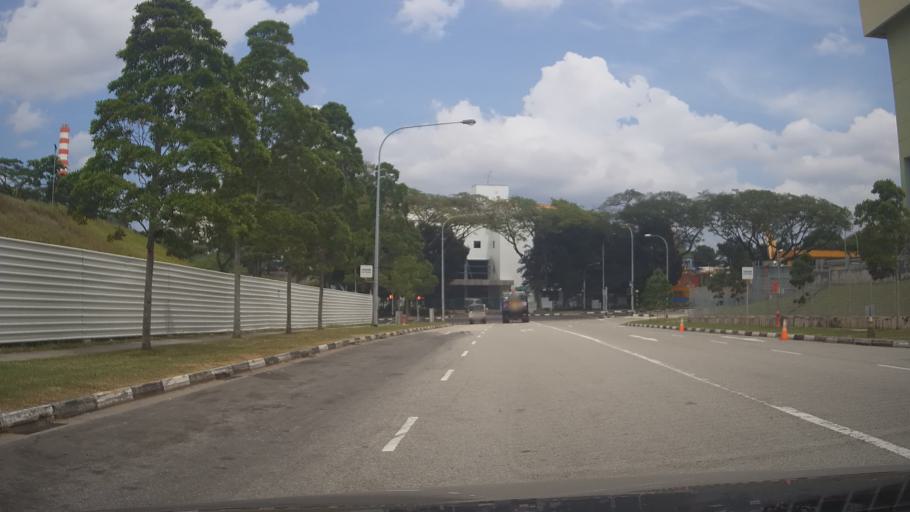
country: MY
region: Johor
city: Johor Bahru
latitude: 1.4572
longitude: 103.7942
